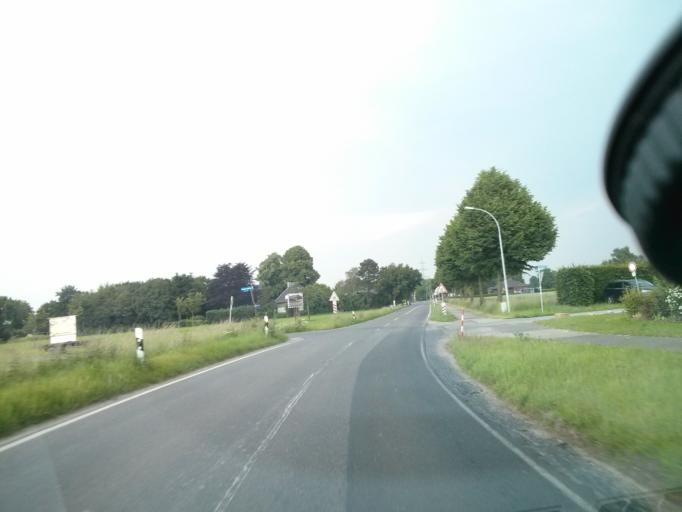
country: DE
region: North Rhine-Westphalia
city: Tonisvorst
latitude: 51.3404
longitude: 6.4981
